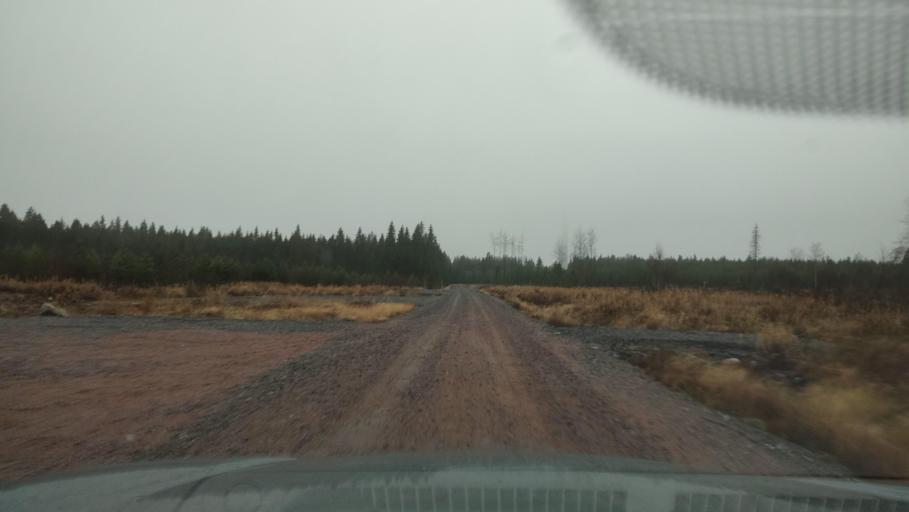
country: FI
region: Southern Ostrobothnia
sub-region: Suupohja
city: Karijoki
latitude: 62.1791
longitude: 21.7239
